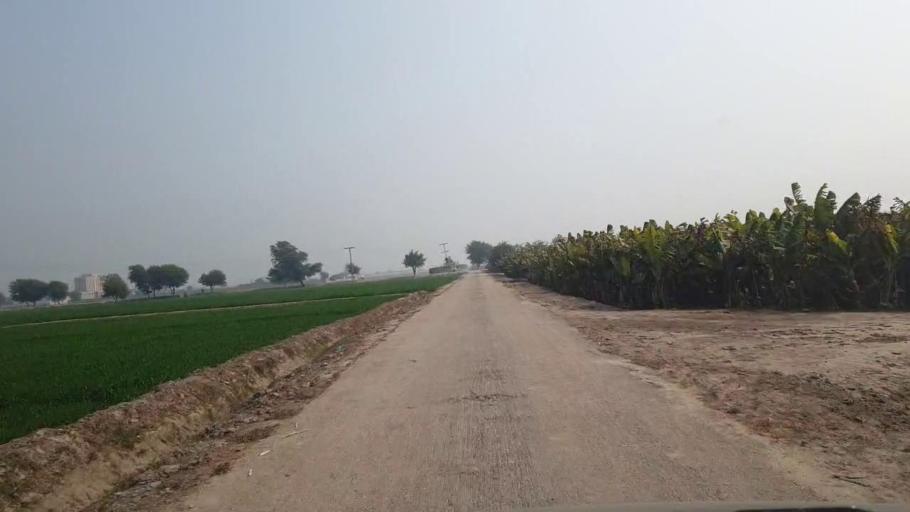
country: PK
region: Sindh
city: Hala
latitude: 25.8253
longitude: 68.4356
